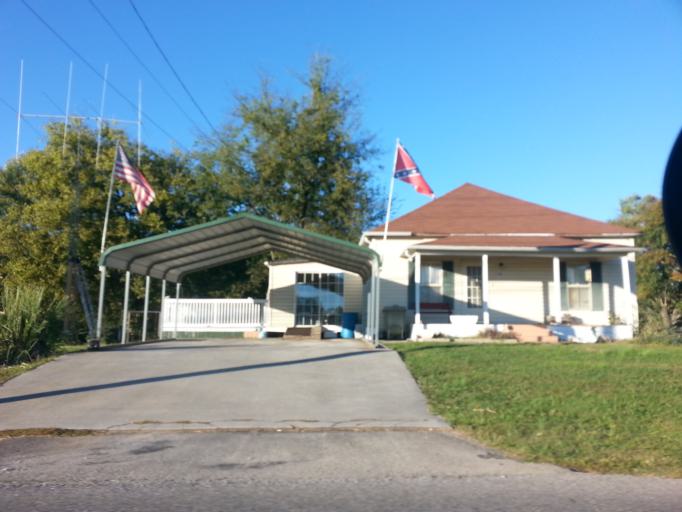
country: US
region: Tennessee
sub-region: Blount County
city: Eagleton Village
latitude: 35.7745
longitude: -83.9422
